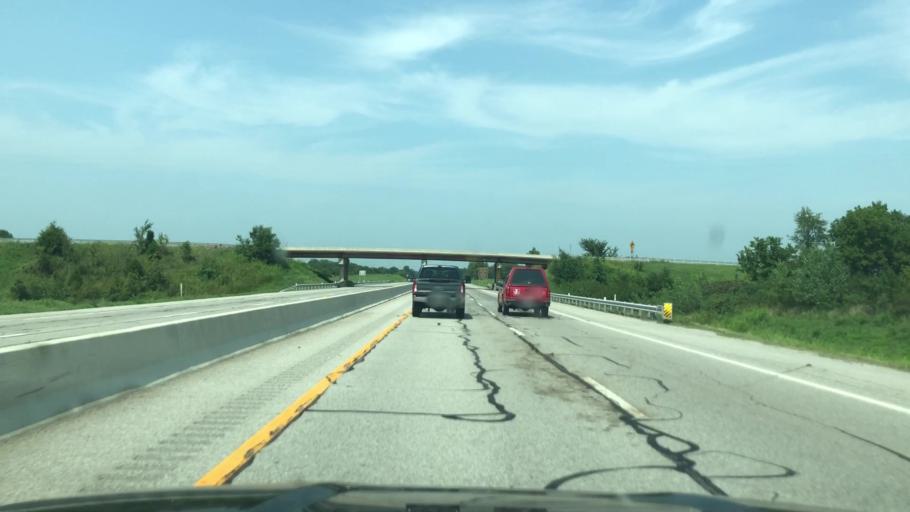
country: US
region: Oklahoma
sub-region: Ottawa County
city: Miami
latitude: 36.8435
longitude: -94.8601
